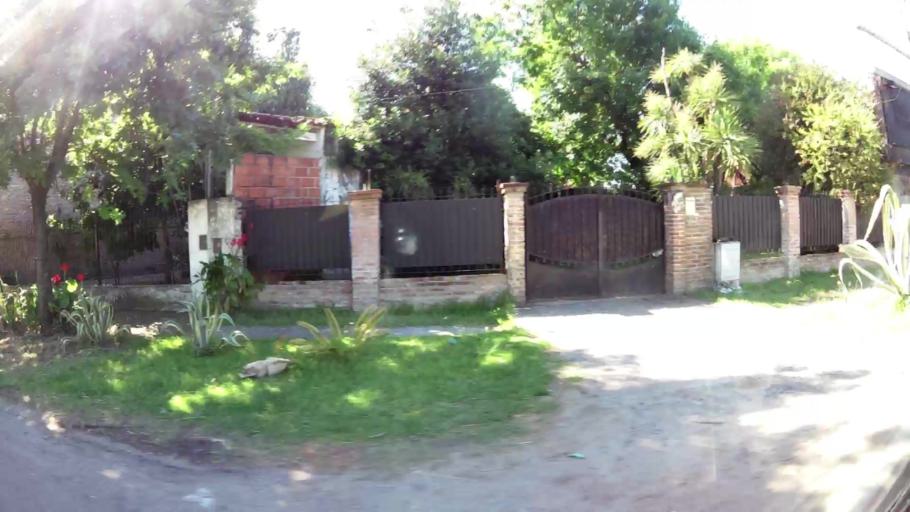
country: AR
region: Buenos Aires
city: Ituzaingo
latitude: -34.6308
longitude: -58.6556
